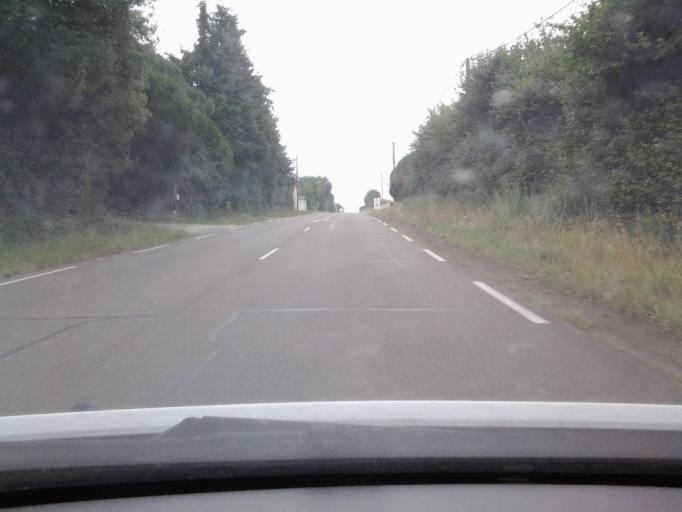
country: FR
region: Pays de la Loire
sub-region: Departement de la Vendee
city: Les Clouzeaux
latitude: 46.6574
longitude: -1.4806
